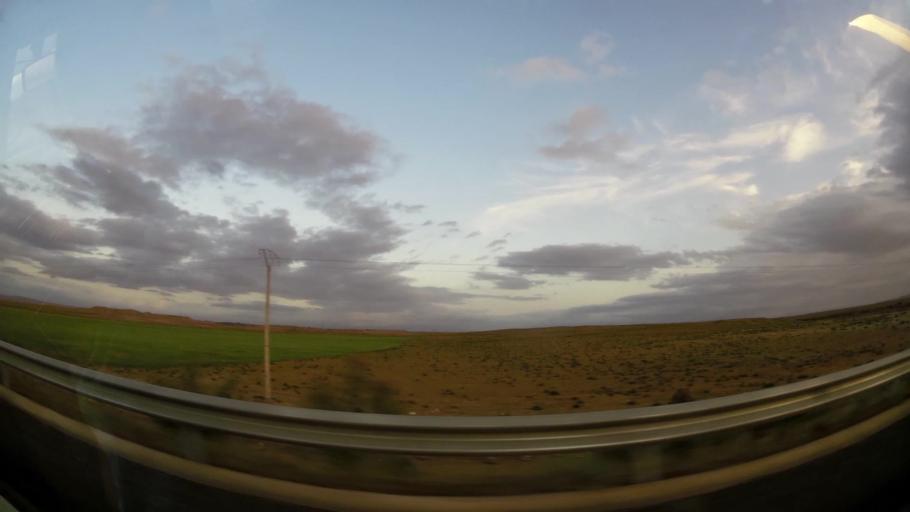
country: MA
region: Oriental
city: Taourirt
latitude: 34.5523
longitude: -2.8508
